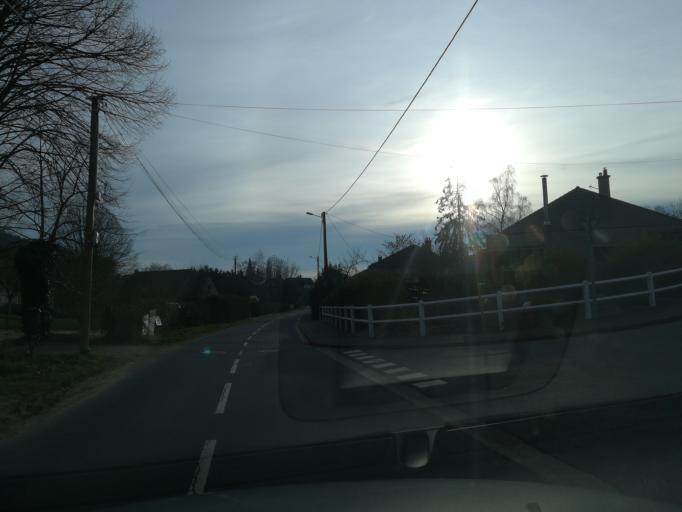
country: FR
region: Haute-Normandie
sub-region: Departement de la Seine-Maritime
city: Saint-Martin-de-Boscherville
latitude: 49.4507
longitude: 0.9699
